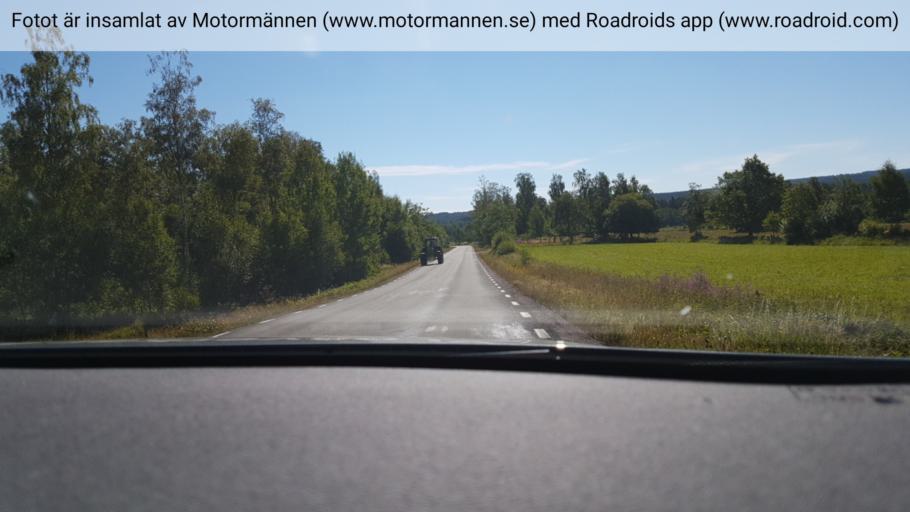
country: SE
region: Vaestra Goetaland
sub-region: Tidaholms Kommun
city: Tidaholm
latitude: 58.1425
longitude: 13.9942
